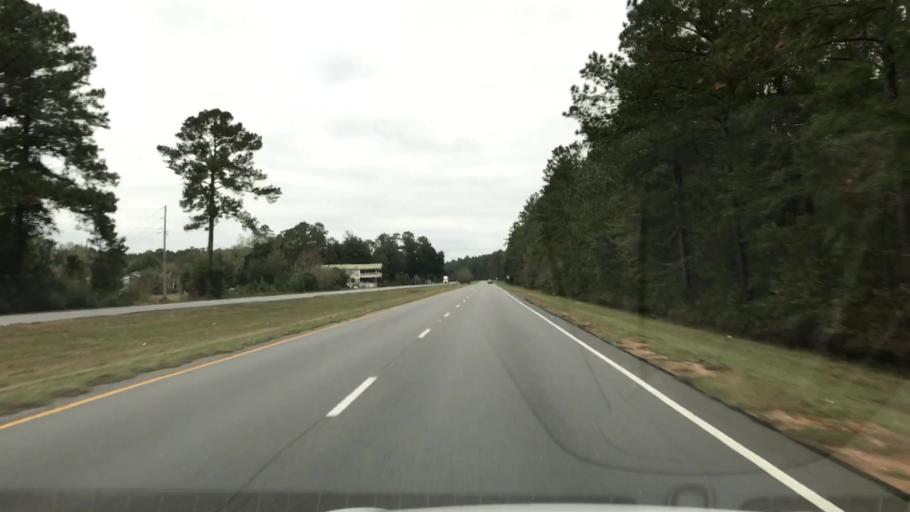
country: US
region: South Carolina
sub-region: Georgetown County
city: Georgetown
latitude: 33.2257
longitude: -79.3776
